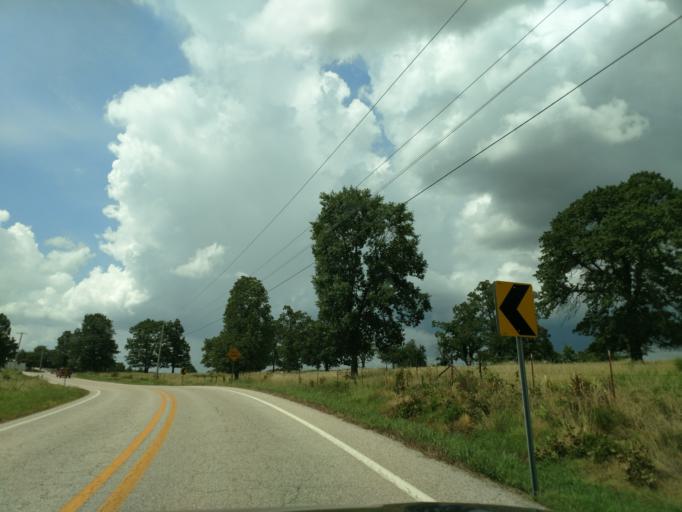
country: US
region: Arkansas
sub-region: Boone County
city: Harrison
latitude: 36.2654
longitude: -93.2306
